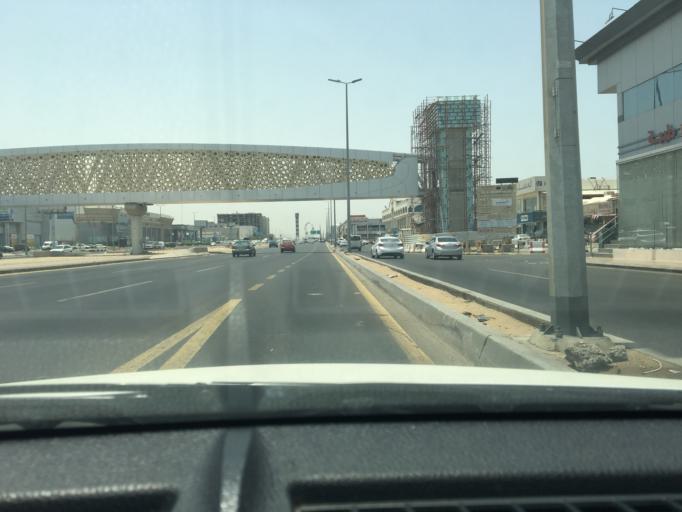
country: SA
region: Makkah
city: Jeddah
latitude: 21.5935
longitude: 39.1738
